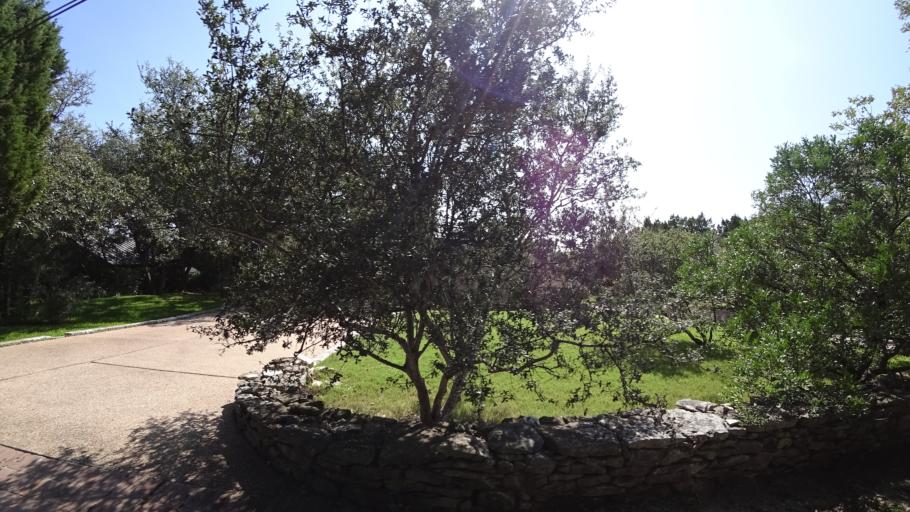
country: US
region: Texas
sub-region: Travis County
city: West Lake Hills
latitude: 30.2967
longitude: -97.8066
